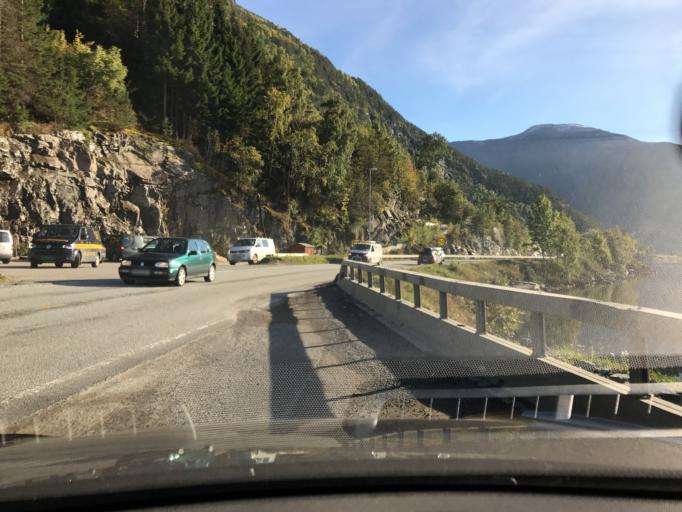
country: NO
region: Sogn og Fjordane
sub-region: Sogndal
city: Sogndalsfjora
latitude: 61.2289
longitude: 7.1251
